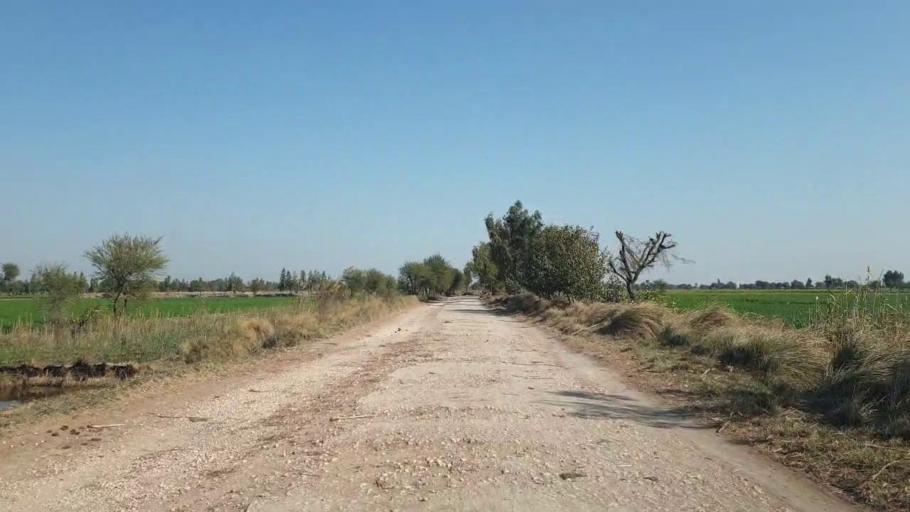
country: PK
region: Sindh
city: Shahdadpur
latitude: 25.9791
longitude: 68.6717
